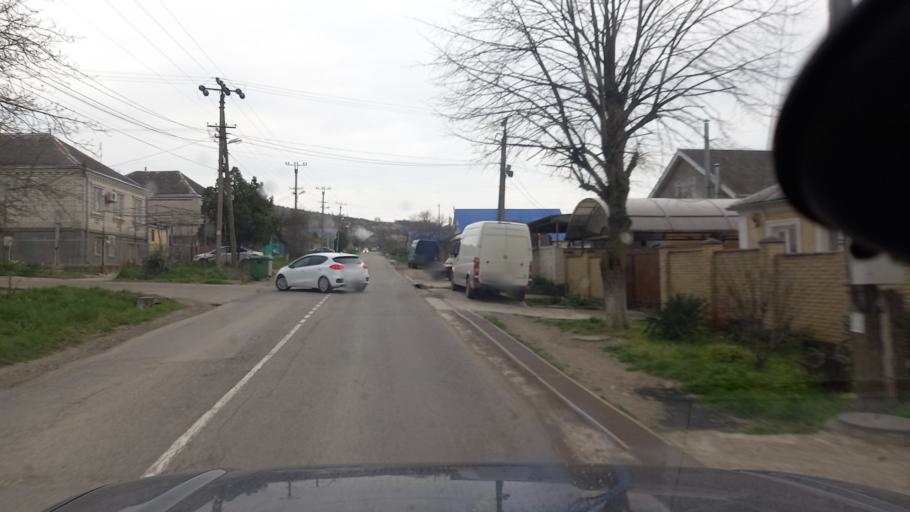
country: RU
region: Krasnodarskiy
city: Sukko
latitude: 44.8506
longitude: 37.4362
